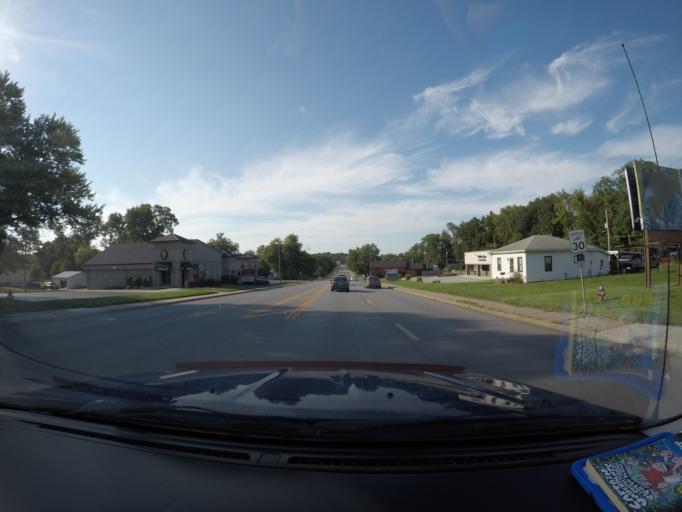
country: US
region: Kansas
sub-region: Leavenworth County
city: Leavenworth
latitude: 39.2896
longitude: -94.9071
